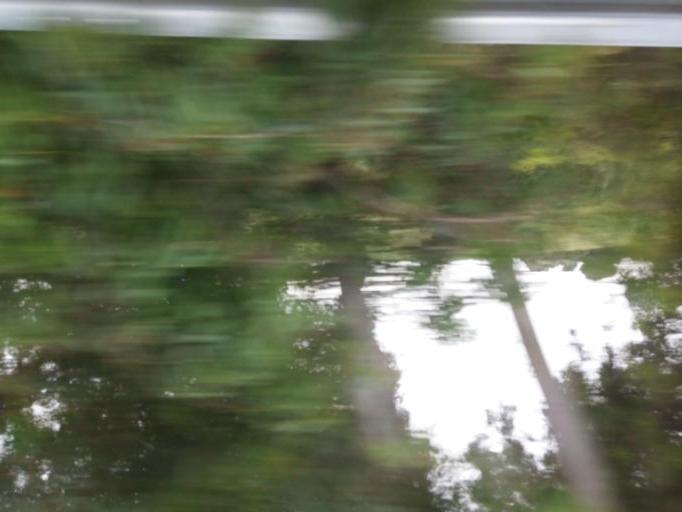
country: DZ
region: Tipaza
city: Tipasa
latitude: 36.5791
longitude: 2.5436
